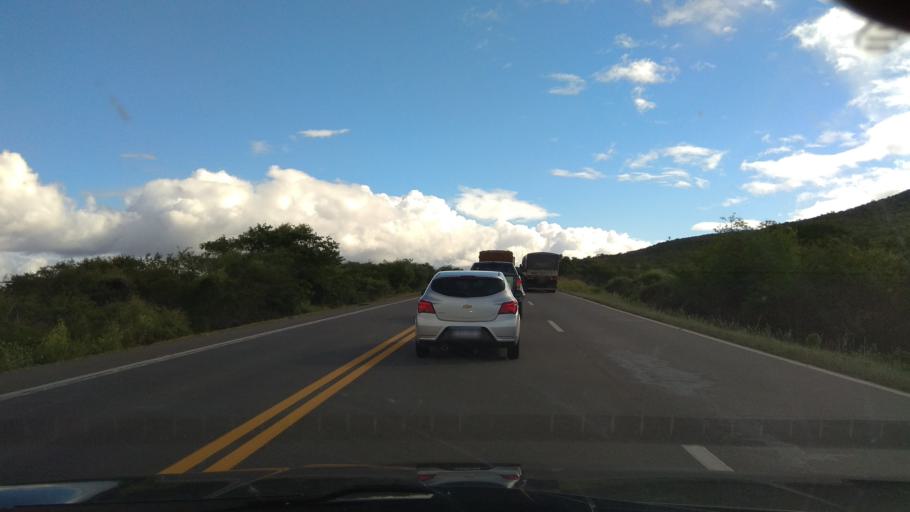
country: BR
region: Bahia
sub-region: Castro Alves
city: Castro Alves
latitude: -12.6508
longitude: -39.6090
